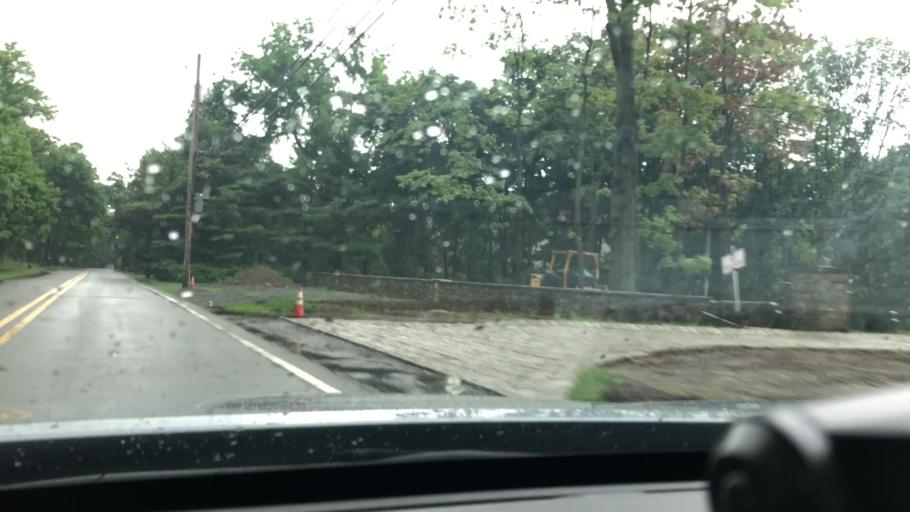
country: US
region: New Jersey
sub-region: Bergen County
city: Woodcliff Lake
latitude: 41.0380
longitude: -74.0808
